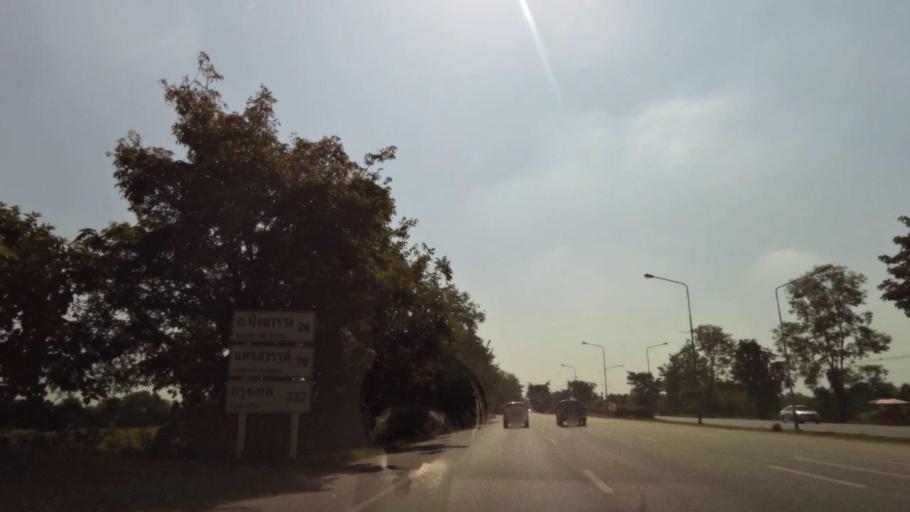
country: TH
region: Phichit
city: Wachira Barami
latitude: 16.4080
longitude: 100.1425
